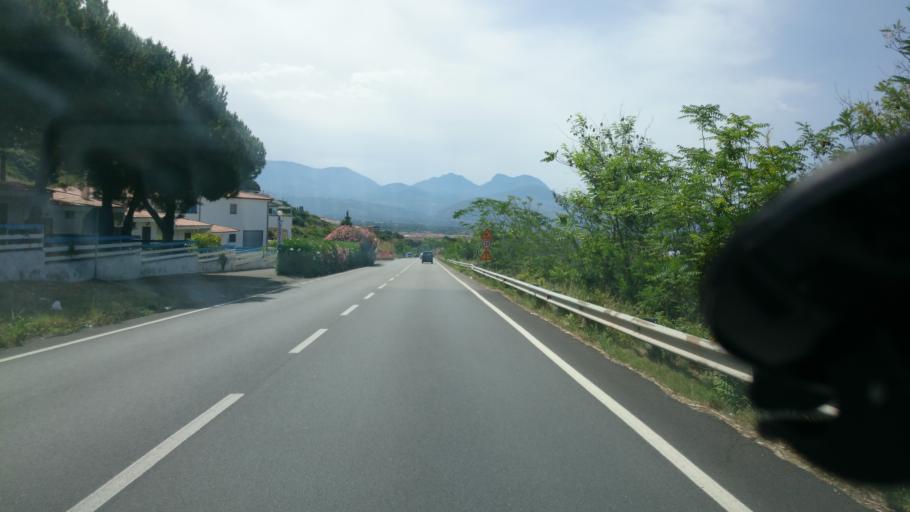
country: IT
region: Calabria
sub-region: Provincia di Cosenza
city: San Nicola Arcella
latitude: 39.8232
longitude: 15.7807
